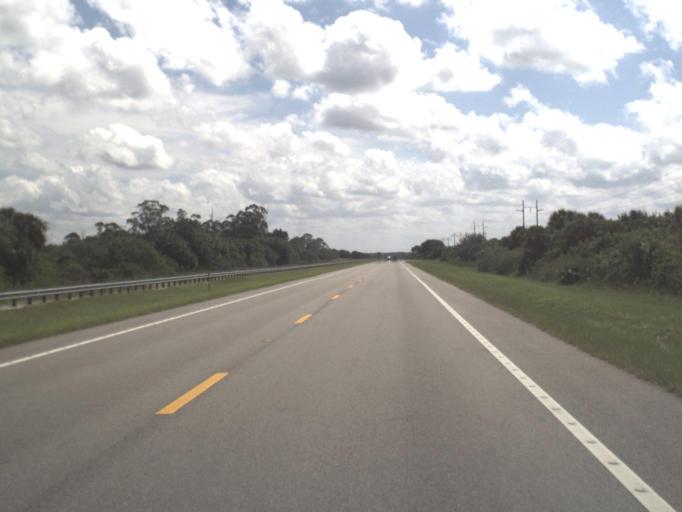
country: US
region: Florida
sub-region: Collier County
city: Immokalee
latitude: 26.3824
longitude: -81.3685
